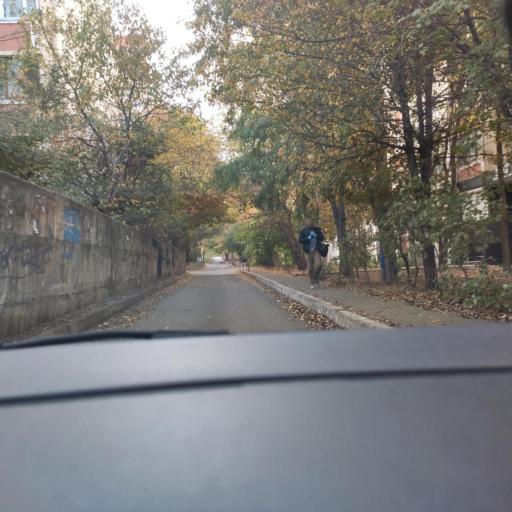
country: RU
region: Voronezj
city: Voronezh
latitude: 51.7062
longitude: 39.1906
